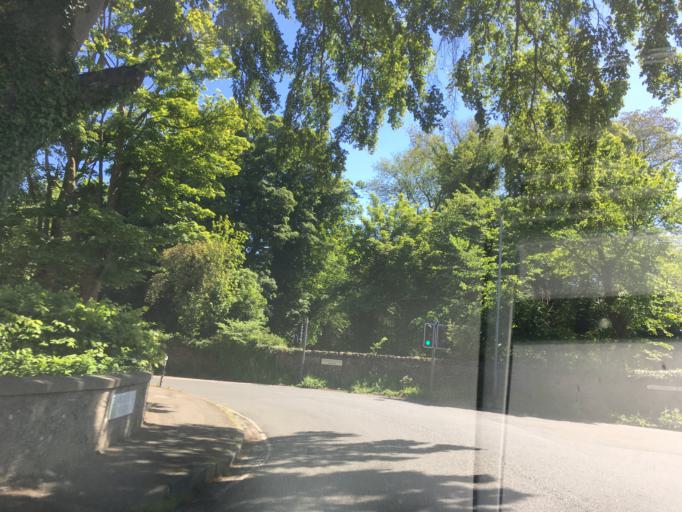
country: GB
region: Scotland
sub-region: Edinburgh
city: Colinton
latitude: 55.9728
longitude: -3.2948
